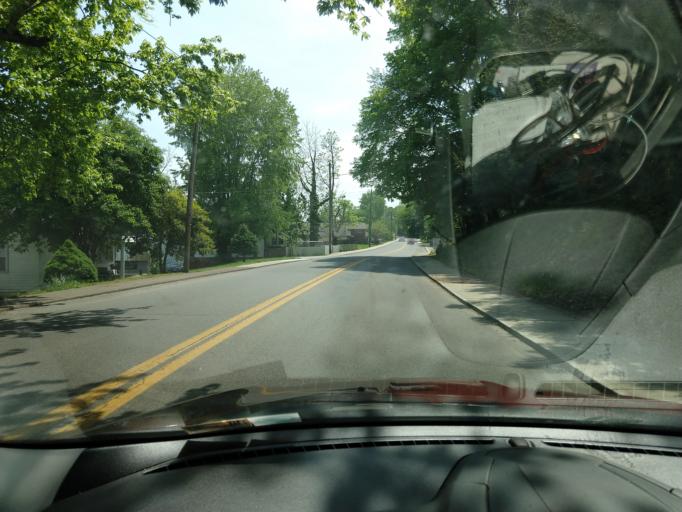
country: US
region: West Virginia
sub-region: Kanawha County
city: Saint Albans
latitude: 38.3823
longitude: -81.8279
